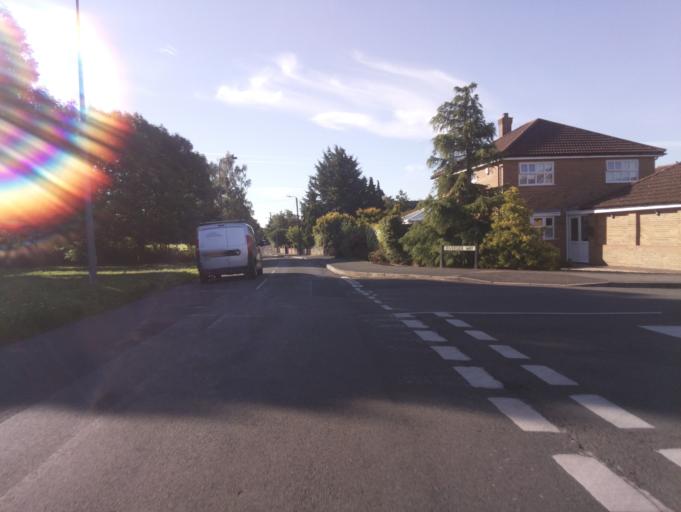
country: GB
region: England
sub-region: South Gloucestershire
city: Kingswood
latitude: 51.4391
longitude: -2.5188
